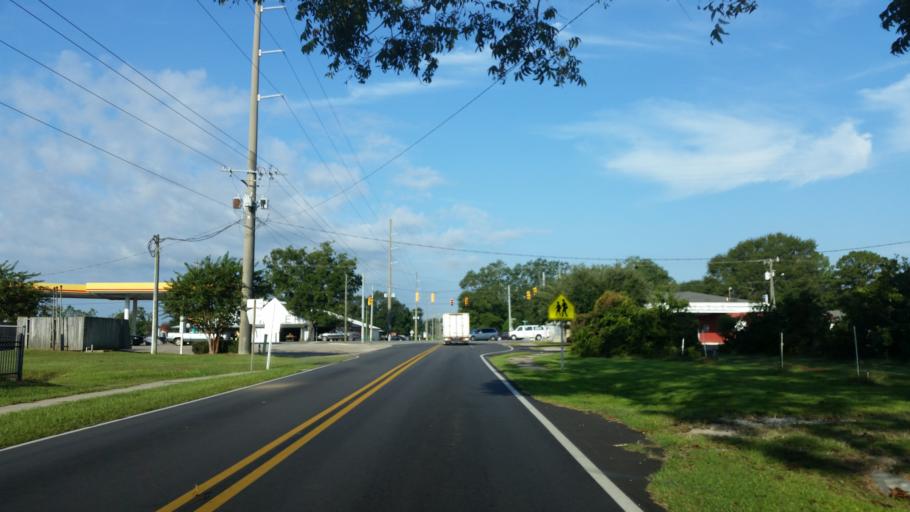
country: US
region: Alabama
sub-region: Baldwin County
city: Loxley
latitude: 30.6184
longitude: -87.7519
